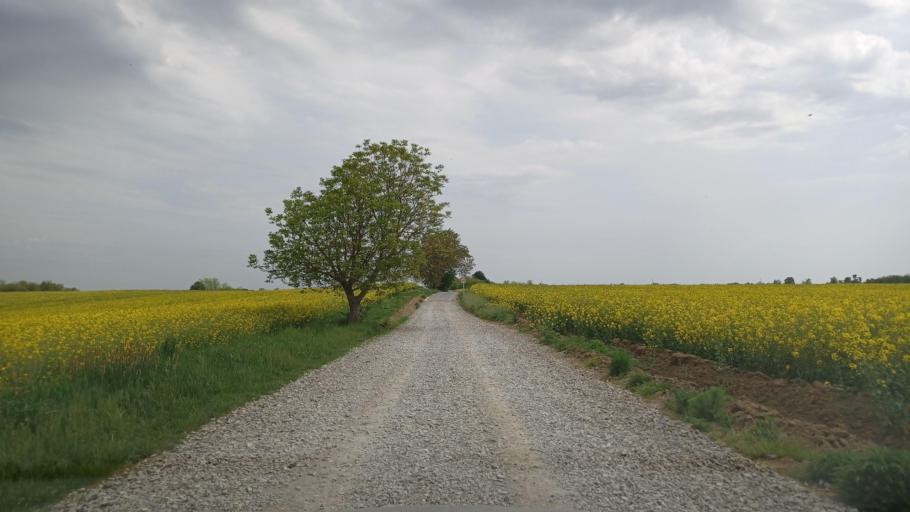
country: HU
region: Baranya
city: Kozarmisleny
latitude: 45.9694
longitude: 18.3492
